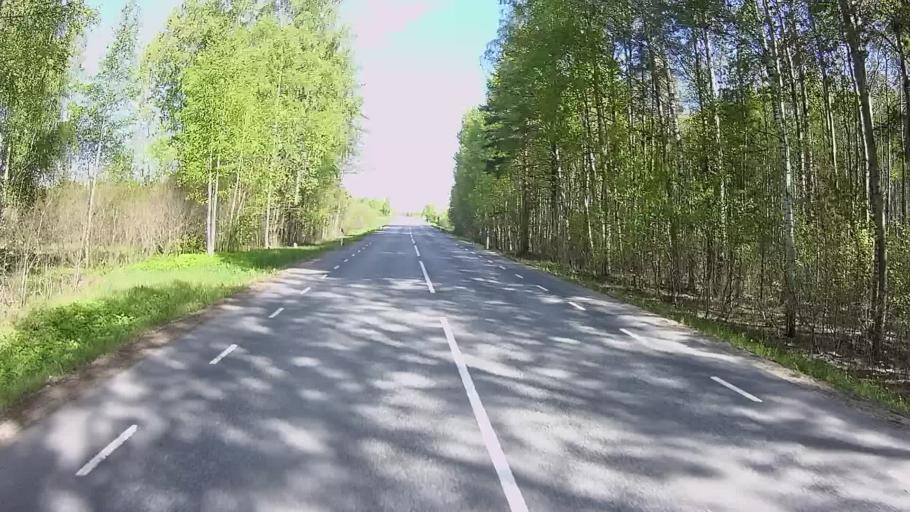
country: EE
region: Polvamaa
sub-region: Raepina vald
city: Rapina
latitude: 58.0613
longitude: 27.5495
